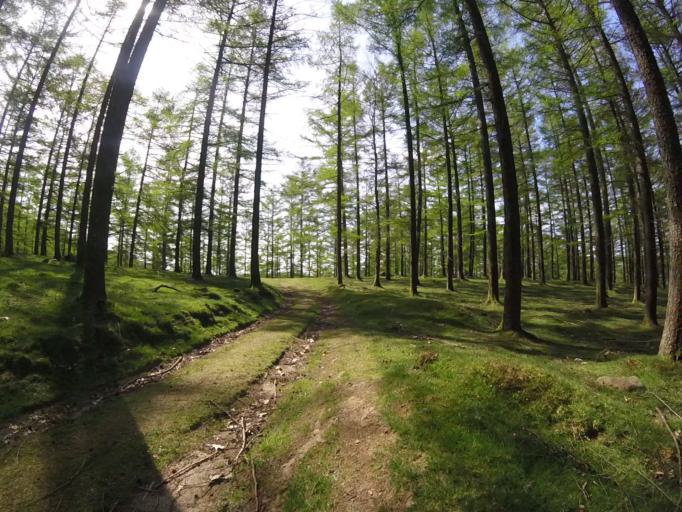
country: ES
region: Navarre
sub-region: Provincia de Navarra
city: Arano
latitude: 43.2556
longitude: -1.8323
